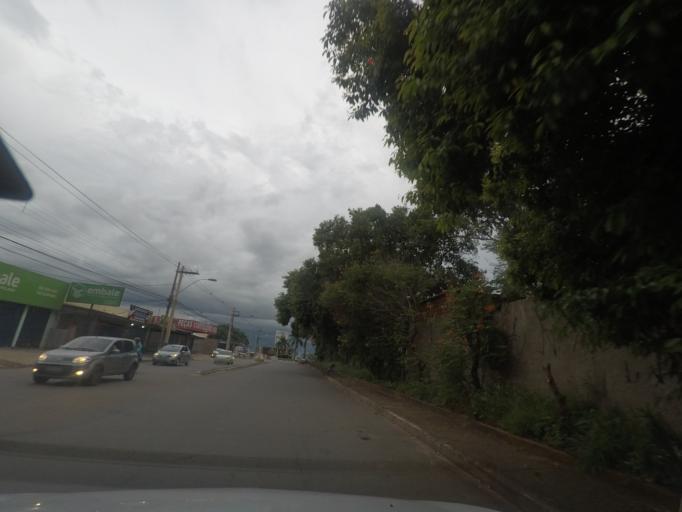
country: BR
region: Goias
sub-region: Goiania
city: Goiania
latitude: -16.7282
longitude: -49.2385
